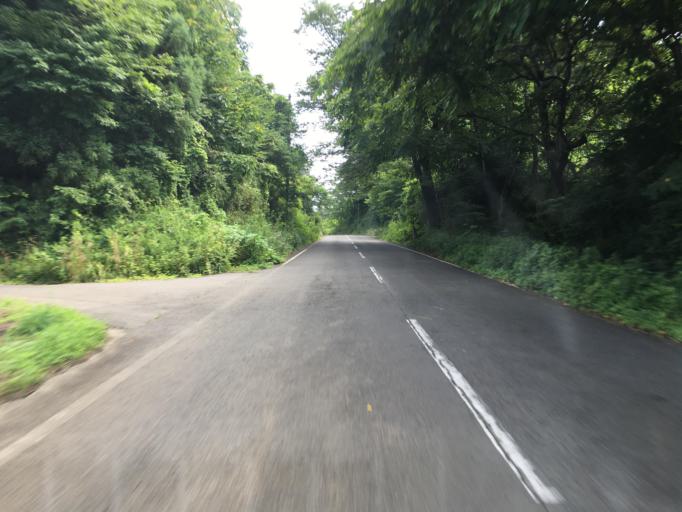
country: JP
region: Fukushima
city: Nihommatsu
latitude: 37.6307
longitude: 140.4552
